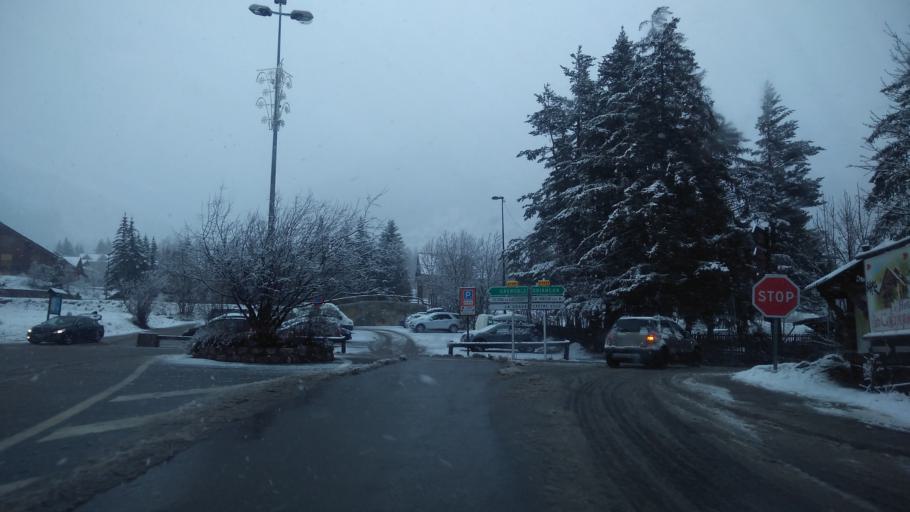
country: FR
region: Provence-Alpes-Cote d'Azur
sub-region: Departement des Hautes-Alpes
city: Le Monetier-les-Bains
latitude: 44.9773
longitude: 6.5046
